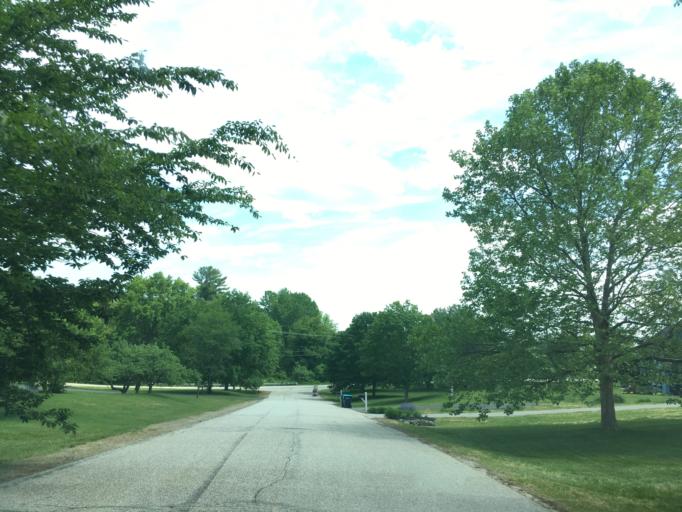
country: US
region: New Hampshire
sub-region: Rockingham County
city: Stratham Station
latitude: 43.0246
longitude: -70.8762
